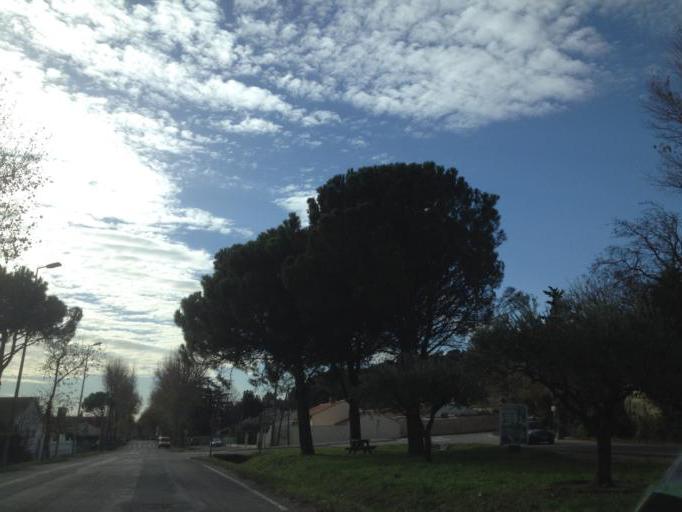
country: FR
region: Provence-Alpes-Cote d'Azur
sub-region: Departement du Vaucluse
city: Bedarrides
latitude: 44.0420
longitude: 4.8849
